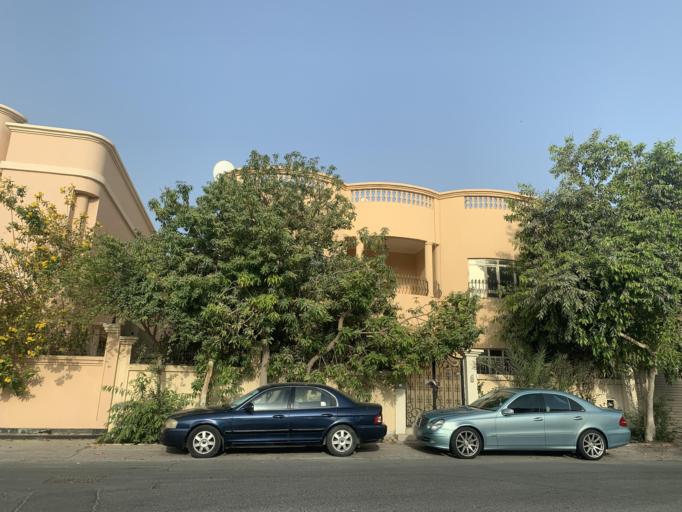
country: BH
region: Northern
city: Madinat `Isa
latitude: 26.1948
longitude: 50.5620
